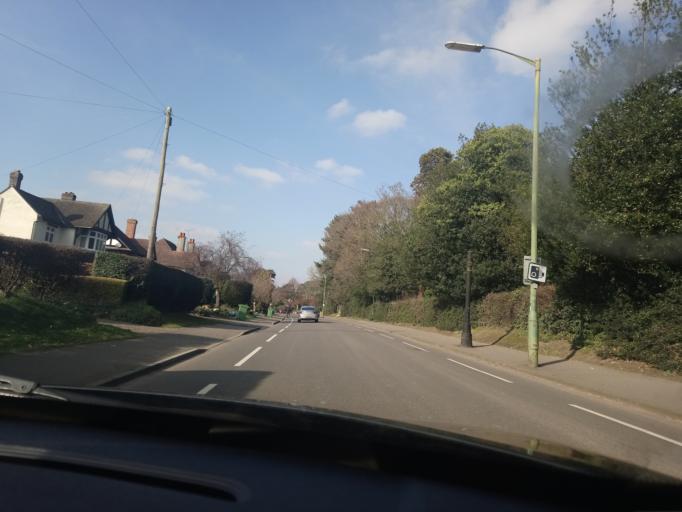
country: GB
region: England
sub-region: Shropshire
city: Shrewsbury
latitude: 52.6990
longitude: -2.7259
